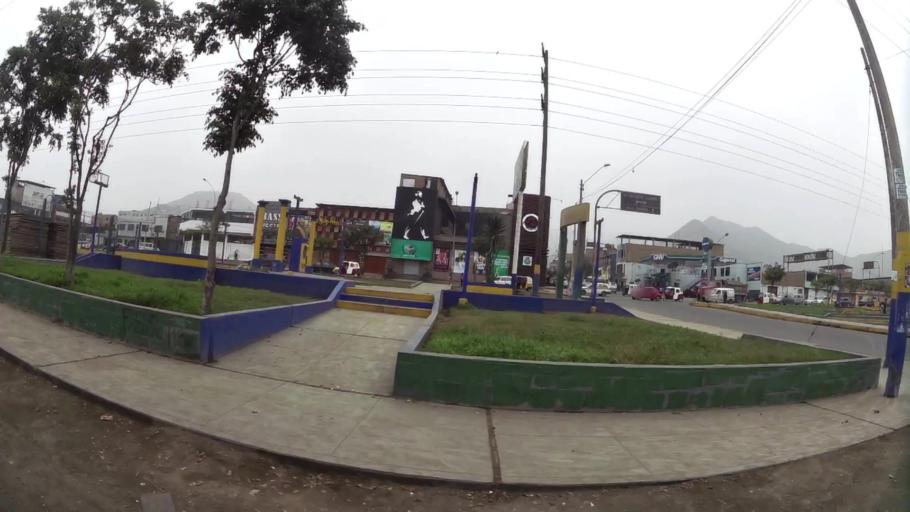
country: PE
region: Lima
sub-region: Lima
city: Surco
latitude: -12.1670
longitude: -76.9499
